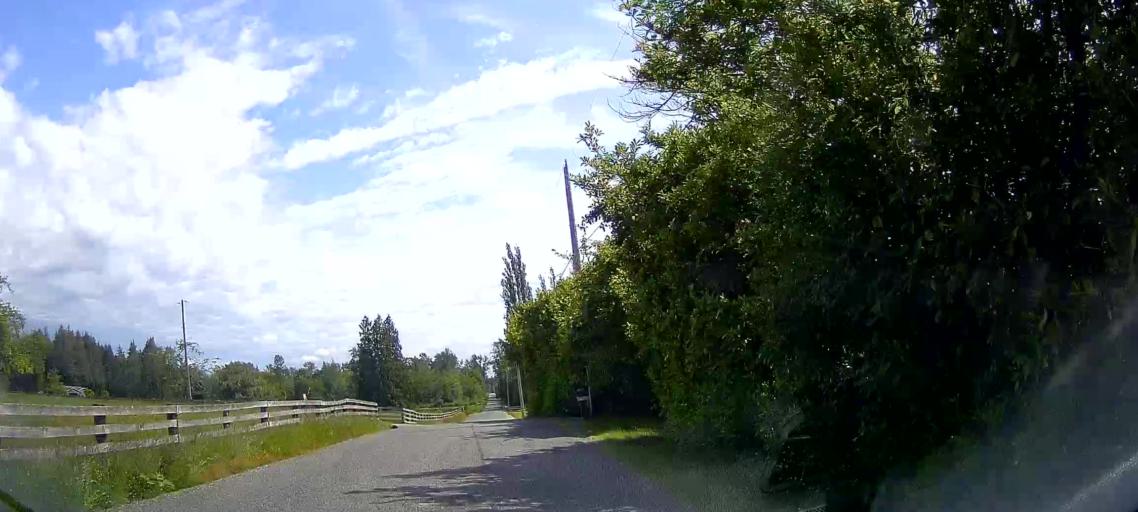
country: US
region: Washington
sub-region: Skagit County
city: Burlington
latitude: 48.5548
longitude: -122.3620
